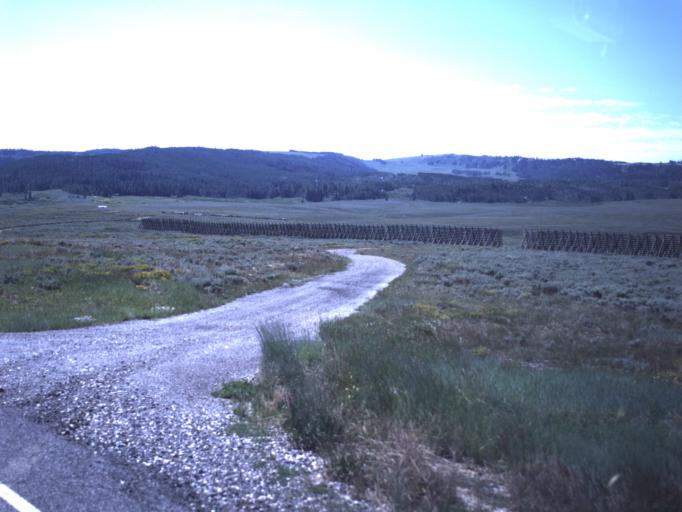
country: US
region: Utah
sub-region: Sanpete County
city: Fairview
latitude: 39.6718
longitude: -111.3097
